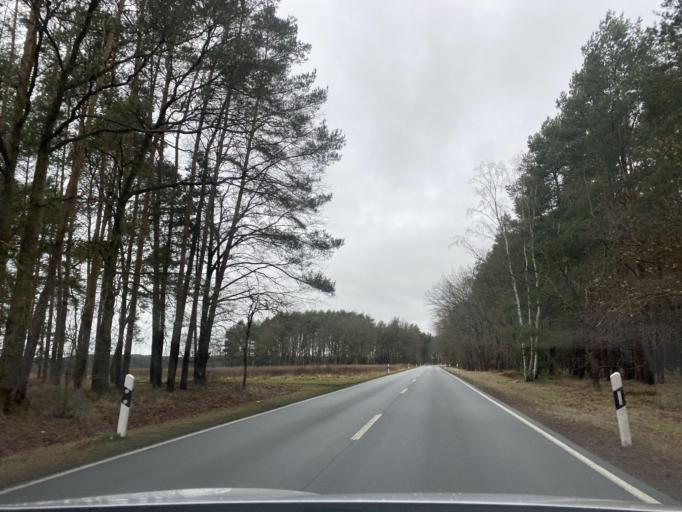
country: DE
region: Saxony
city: Rothenburg
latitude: 51.3920
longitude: 14.9506
